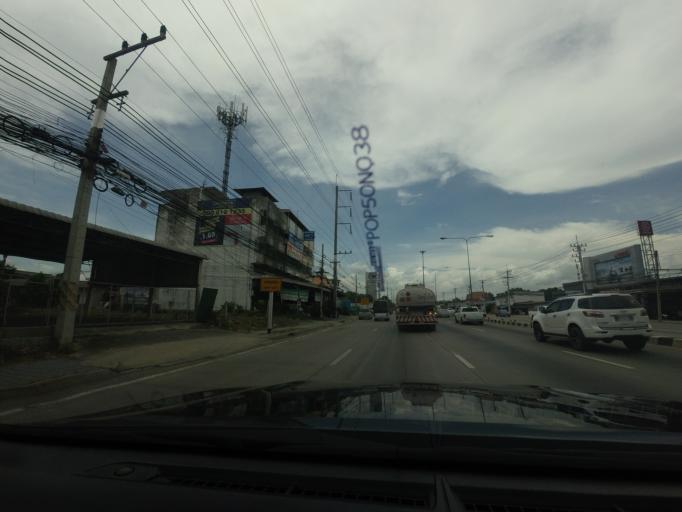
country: TH
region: Nakhon Pathom
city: Nakhon Pathom
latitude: 13.8345
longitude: 100.0332
